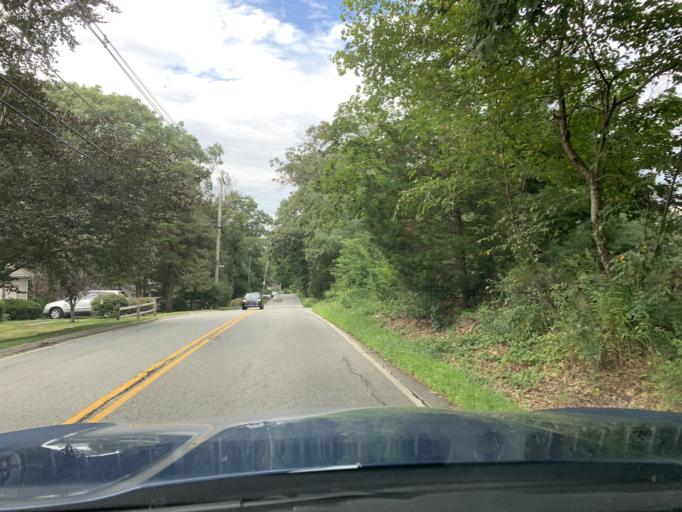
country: US
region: Rhode Island
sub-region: Kent County
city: East Greenwich
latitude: 41.6256
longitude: -71.4483
